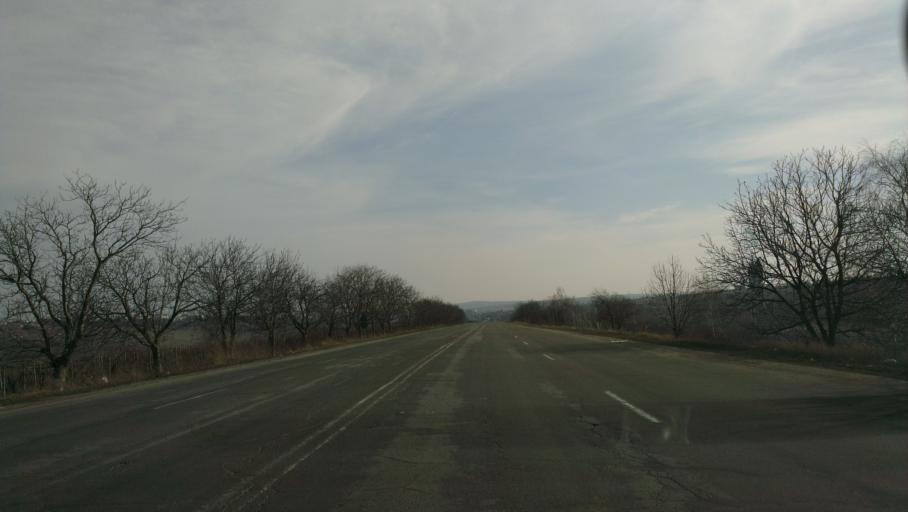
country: MD
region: Laloveni
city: Ialoveni
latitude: 46.9837
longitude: 28.7452
